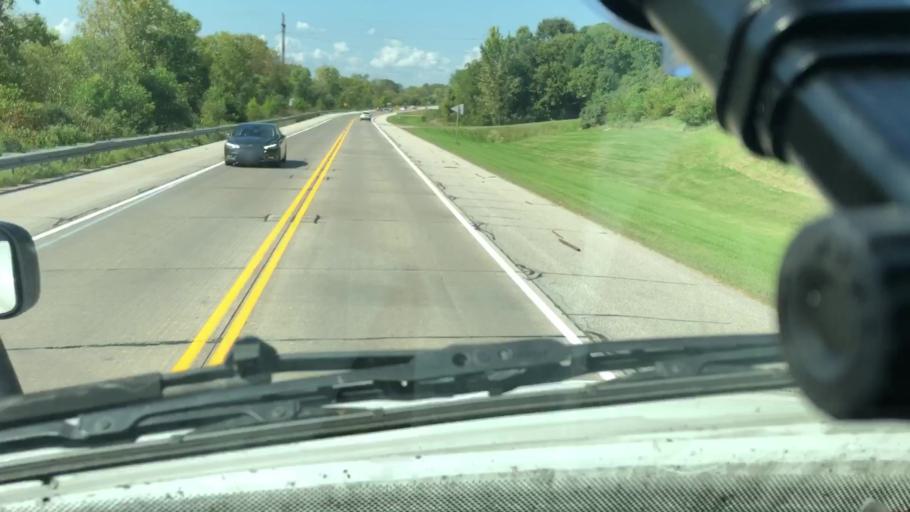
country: US
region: Minnesota
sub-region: Winona County
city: Winona
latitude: 44.0714
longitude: -91.6203
